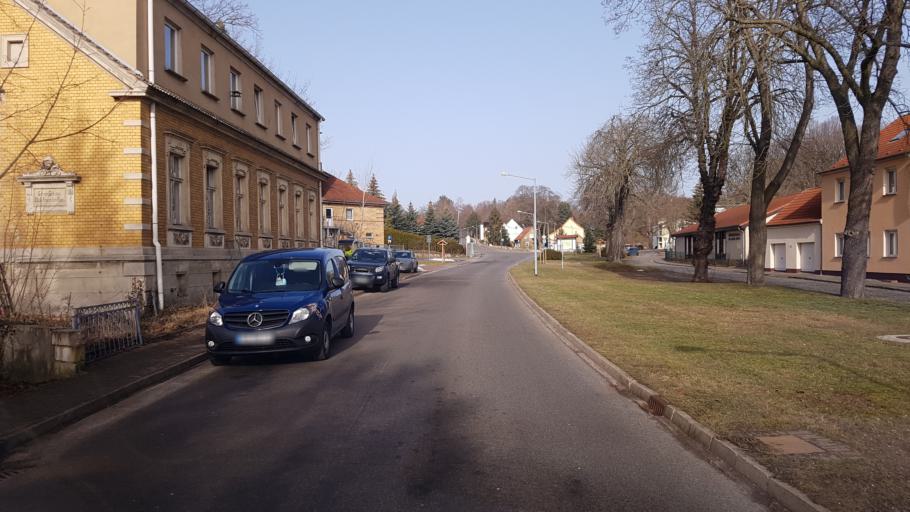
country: DE
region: Brandenburg
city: Schwarzheide
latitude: 51.5247
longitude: 13.8286
